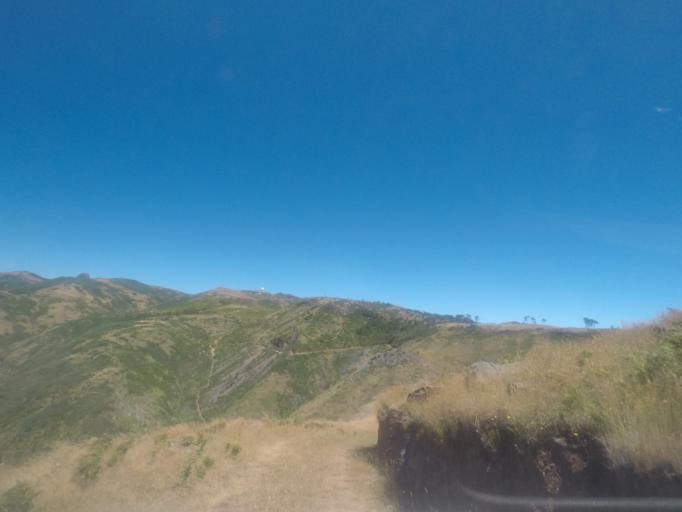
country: PT
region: Madeira
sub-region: Funchal
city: Nossa Senhora do Monte
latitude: 32.7117
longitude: -16.9139
